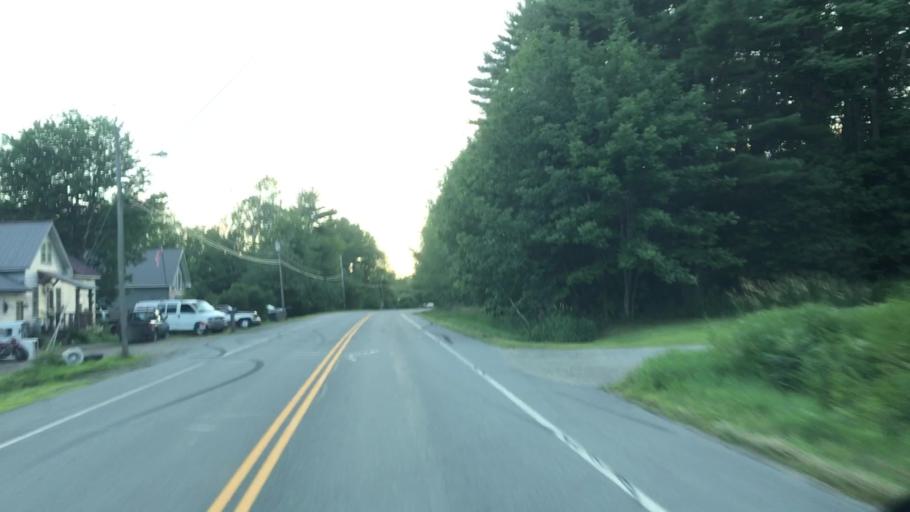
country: US
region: Maine
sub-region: Penobscot County
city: Lincoln
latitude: 45.3743
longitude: -68.4696
